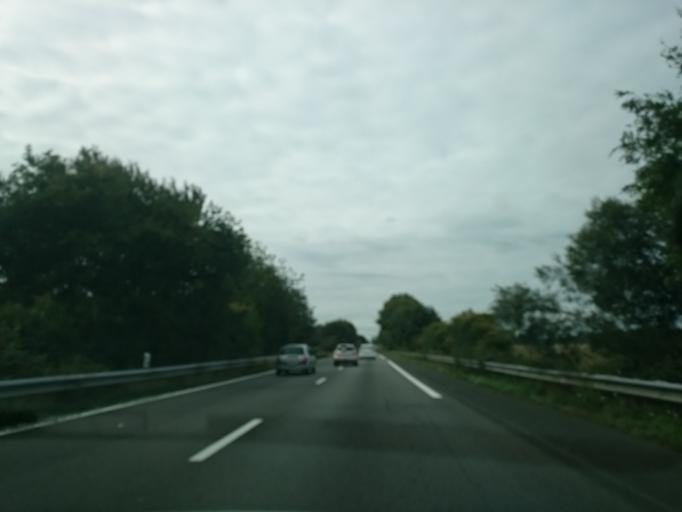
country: FR
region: Pays de la Loire
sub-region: Departement de la Loire-Atlantique
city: Jans
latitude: 47.6194
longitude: -1.6381
